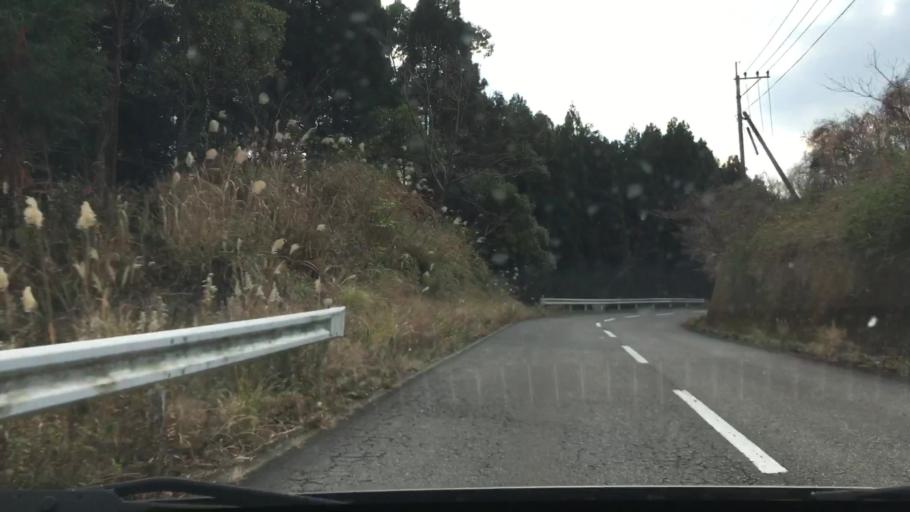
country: JP
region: Miyazaki
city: Nichinan
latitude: 31.6625
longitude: 131.3220
